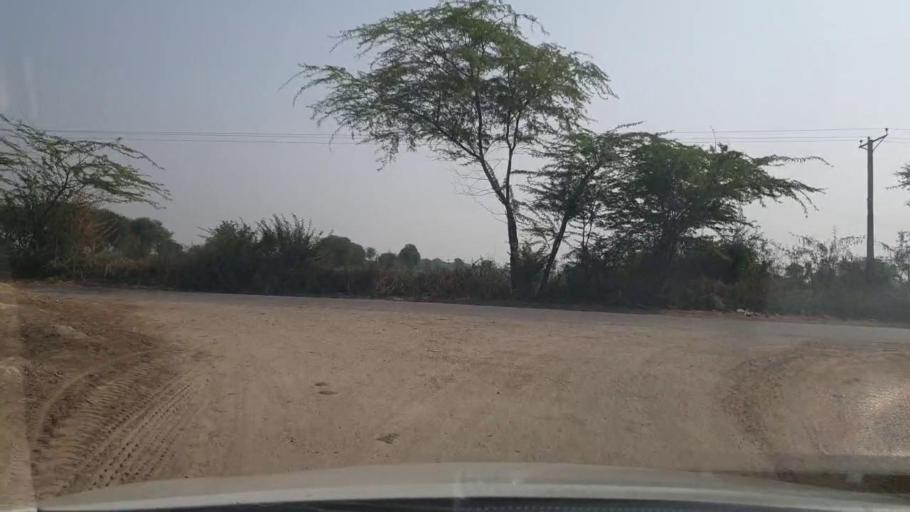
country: PK
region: Sindh
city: Umarkot
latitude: 25.4226
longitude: 69.7275
